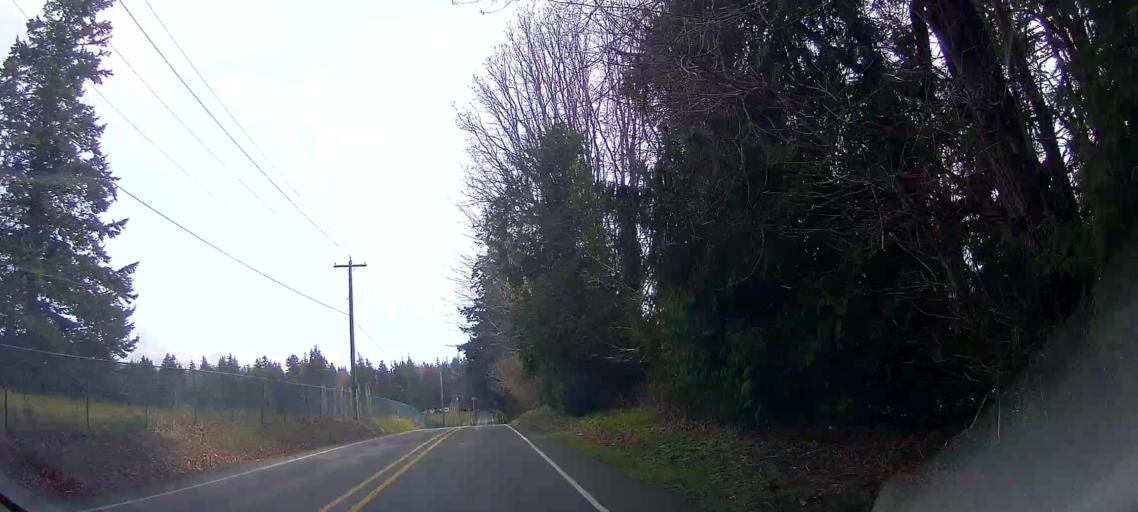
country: US
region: Washington
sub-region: Island County
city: Langley
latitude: 48.1067
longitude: -122.4249
